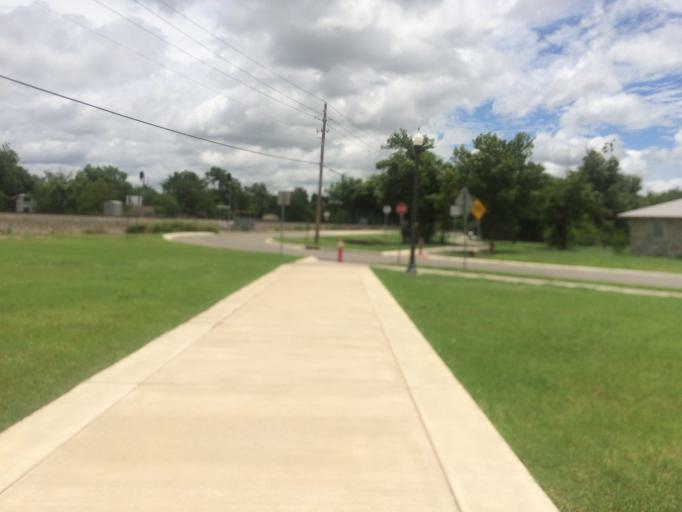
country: US
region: Oklahoma
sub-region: Cleveland County
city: Norman
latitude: 35.2322
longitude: -97.4515
